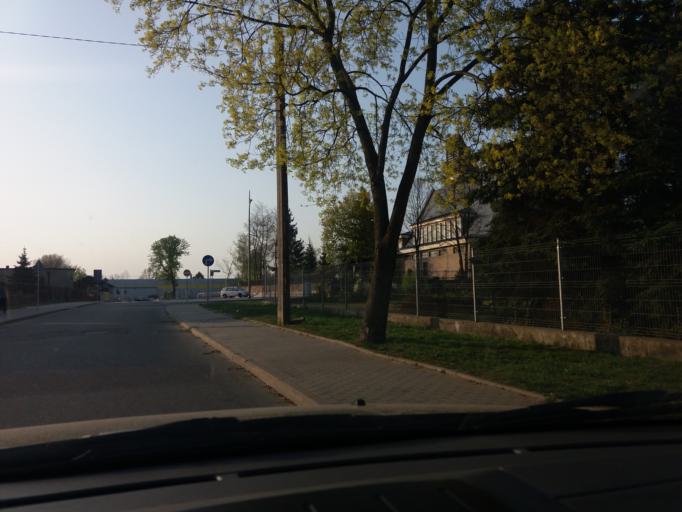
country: PL
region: Masovian Voivodeship
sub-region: Powiat mlawski
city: Mlawa
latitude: 53.1272
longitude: 20.3551
